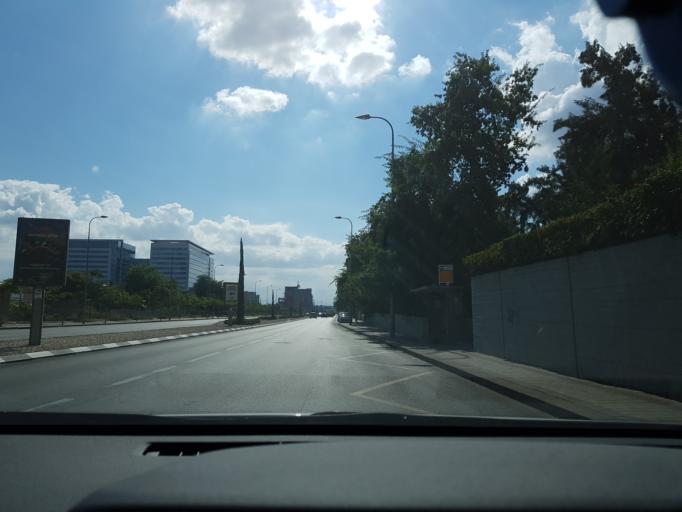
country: IL
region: Tel Aviv
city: Holon
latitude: 32.0100
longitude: 34.7950
